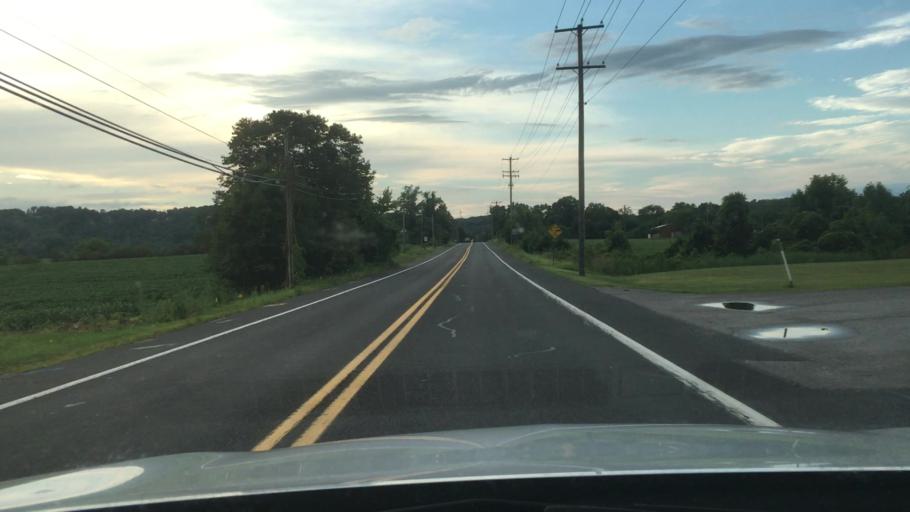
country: US
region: Pennsylvania
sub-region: York County
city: Dover
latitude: 40.0122
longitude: -76.8609
